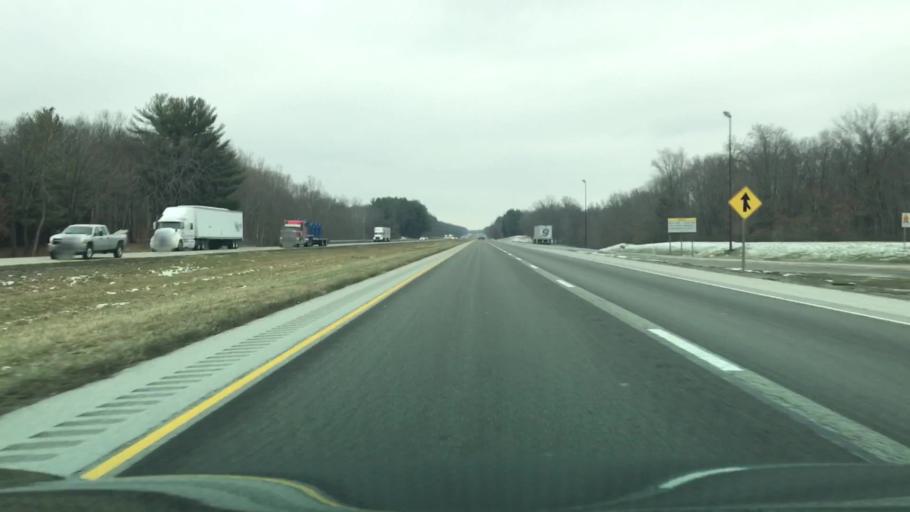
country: US
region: Illinois
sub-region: Franklin County
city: Benton
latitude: 38.0322
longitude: -88.9252
